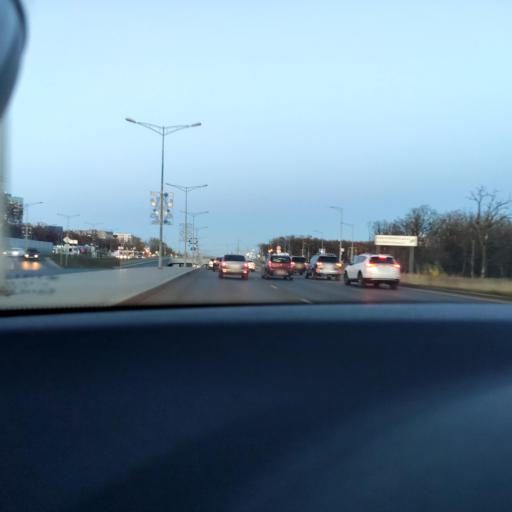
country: RU
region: Samara
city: Petra-Dubrava
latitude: 53.2720
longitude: 50.2609
